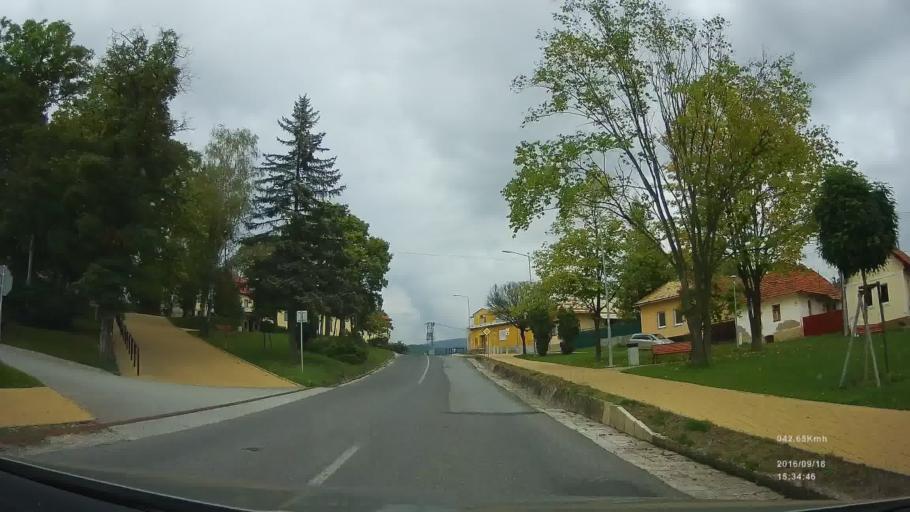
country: SK
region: Kosicky
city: Spisska Nova Ves
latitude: 49.0016
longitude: 20.4639
